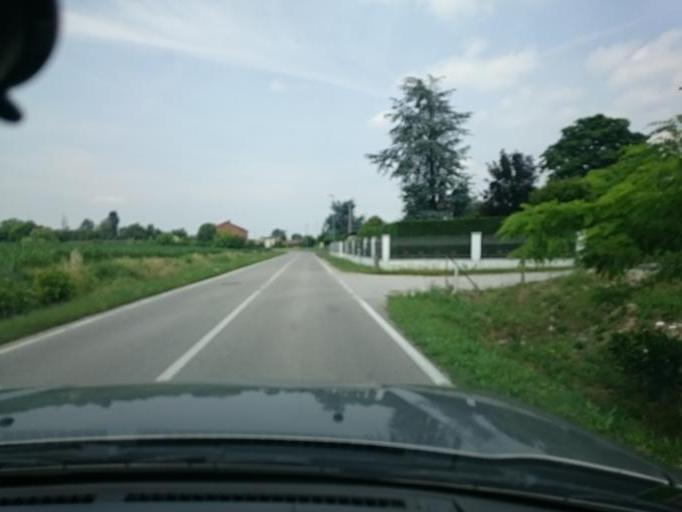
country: IT
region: Veneto
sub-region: Provincia di Padova
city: Sant'Angelo di Piove di Sacco
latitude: 45.3184
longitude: 11.9881
